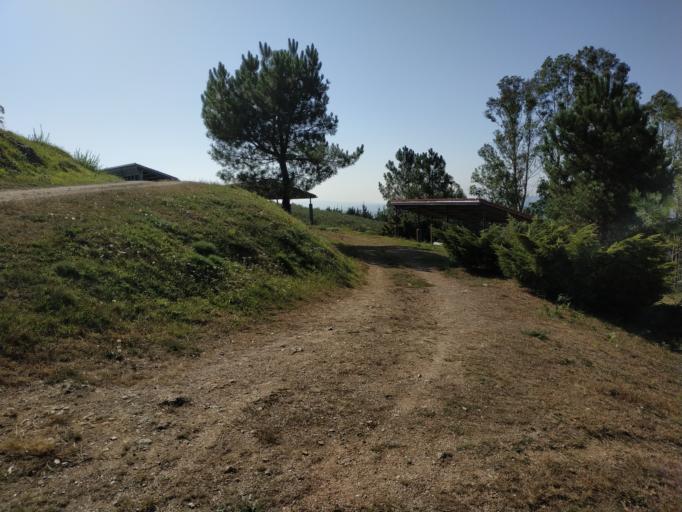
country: ES
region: Galicia
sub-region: Provincia da Coruna
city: Laracha
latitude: 43.2298
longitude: -8.5357
